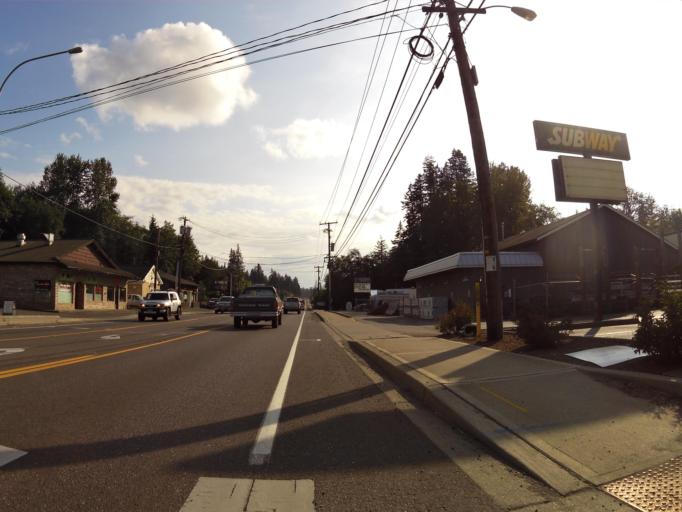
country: US
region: Washington
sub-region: Mason County
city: Belfair
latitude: 47.4504
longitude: -122.8279
